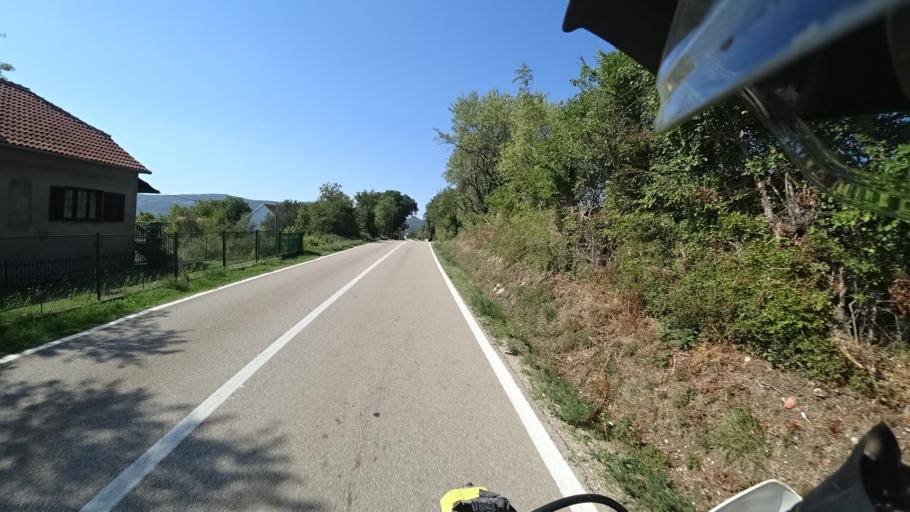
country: HR
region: Sibensko-Kniniska
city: Drnis
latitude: 43.8740
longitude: 16.1980
